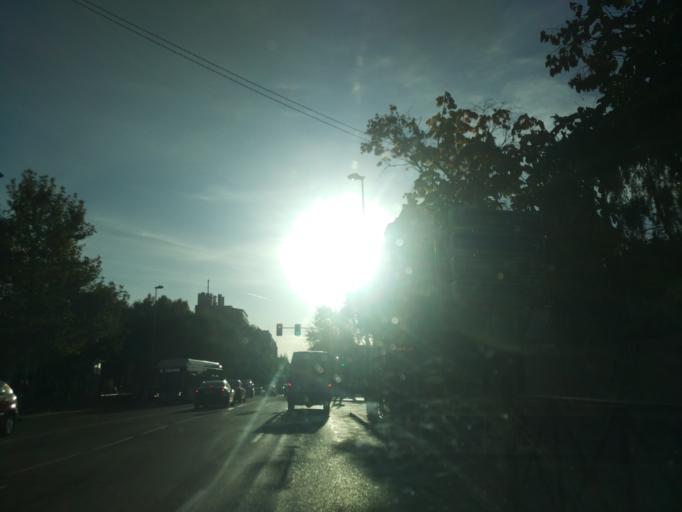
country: ES
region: Madrid
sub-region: Provincia de Madrid
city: Carabanchel
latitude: 40.3890
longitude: -3.7311
